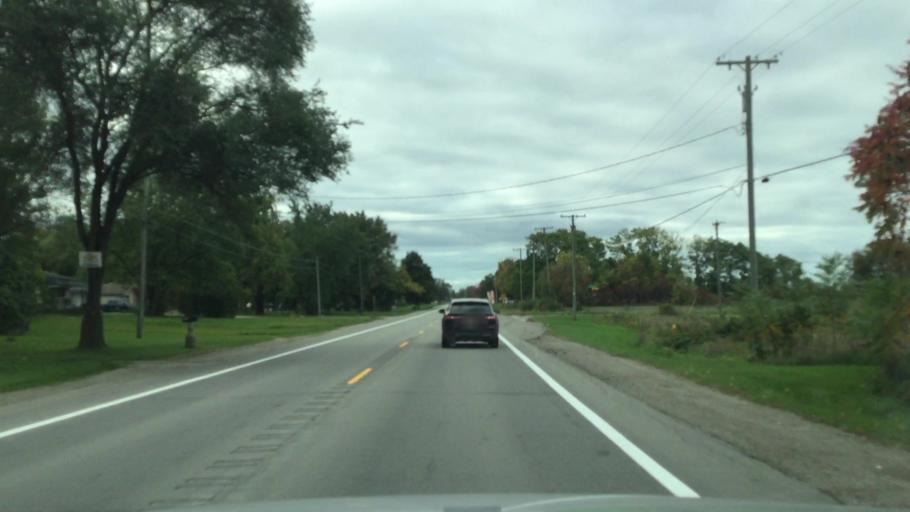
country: US
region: Michigan
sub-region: Macomb County
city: Richmond
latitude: 42.8334
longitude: -82.7615
